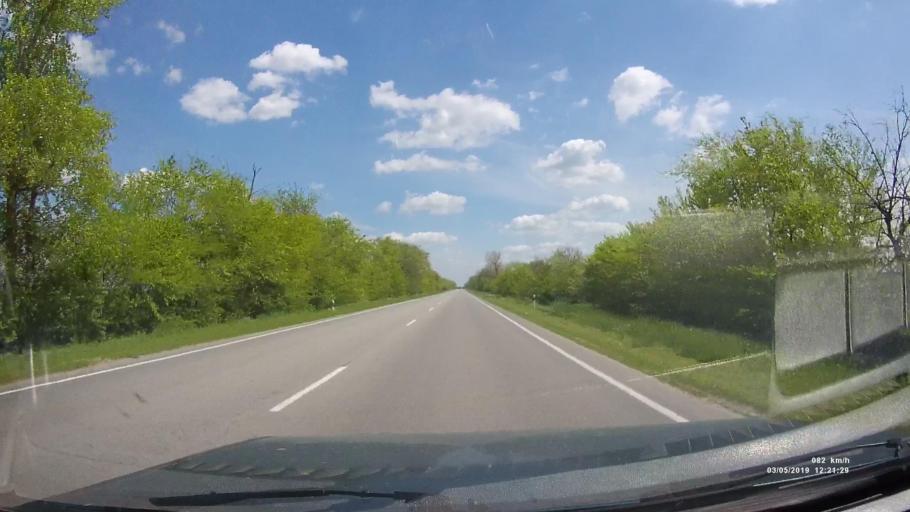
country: RU
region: Rostov
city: Melikhovskaya
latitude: 47.4053
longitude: 40.6395
